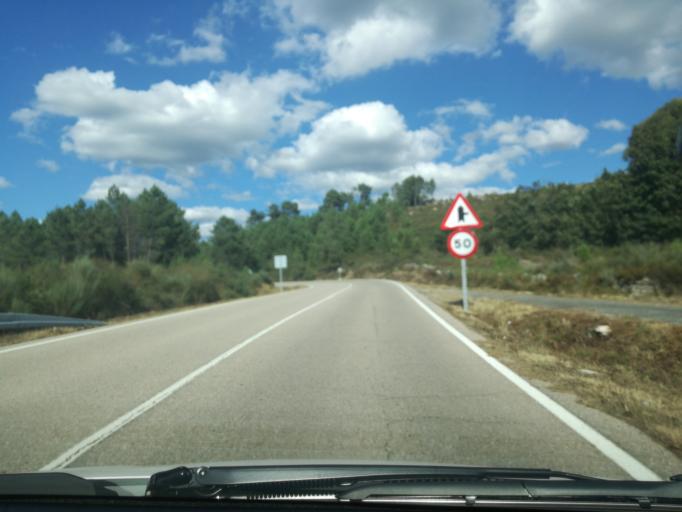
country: ES
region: Galicia
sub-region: Provincia de Ourense
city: Lobios
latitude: 41.8847
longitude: -8.0973
